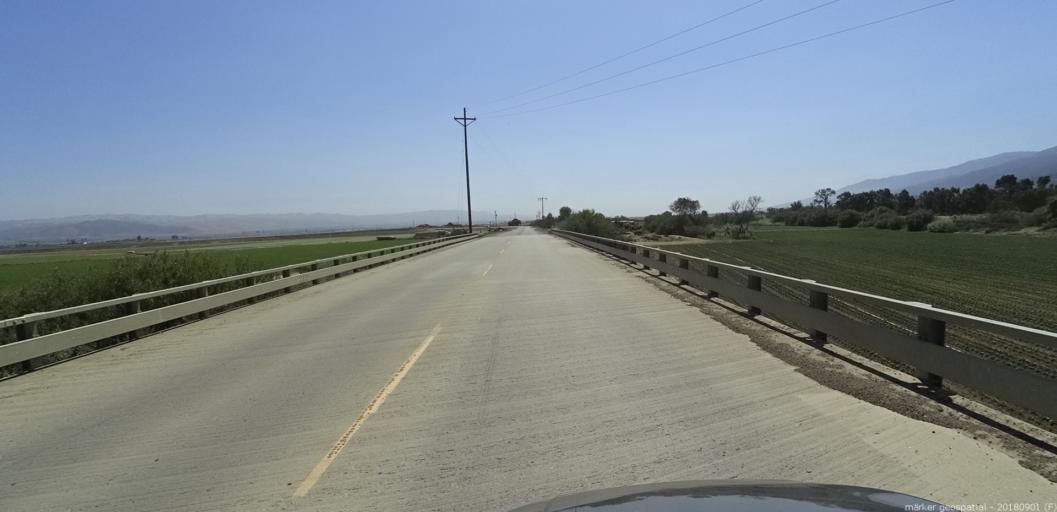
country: US
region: California
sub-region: Monterey County
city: Chualar
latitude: 36.5553
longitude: -121.5475
